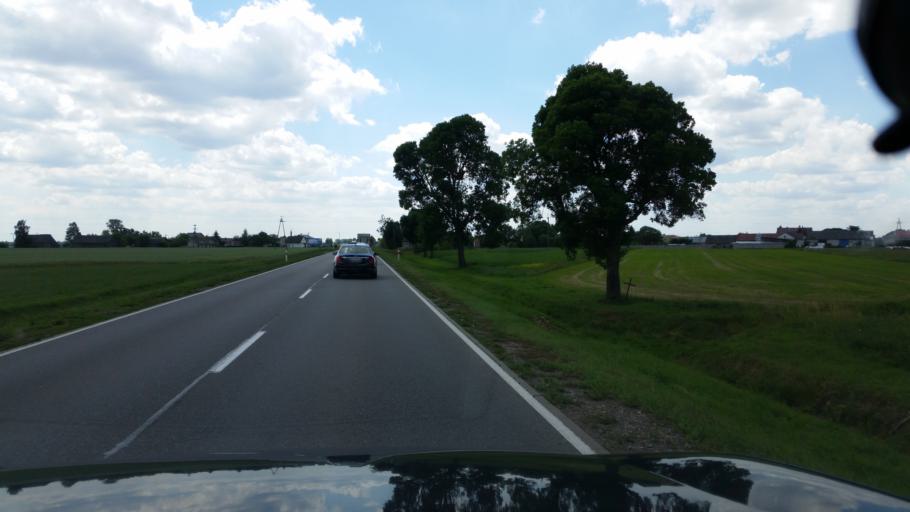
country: PL
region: Masovian Voivodeship
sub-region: Powiat ostrolecki
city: Czerwin
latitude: 52.9417
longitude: 21.8859
